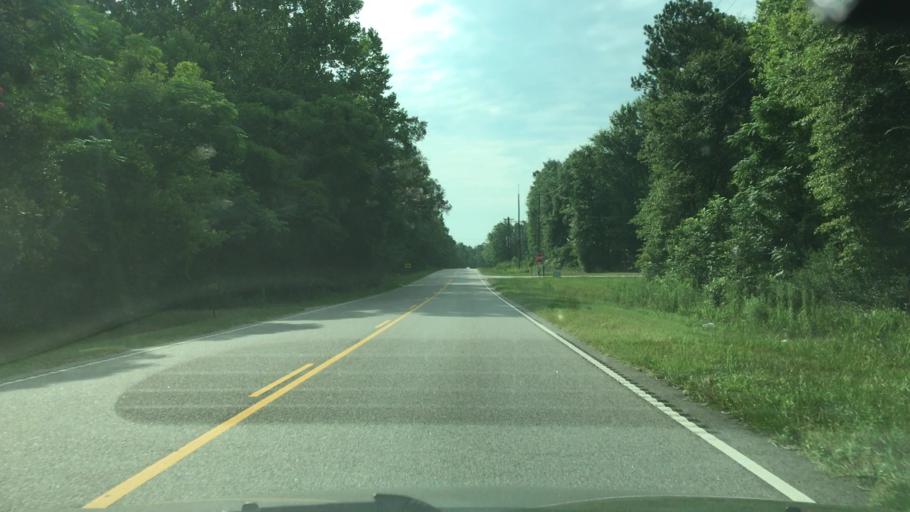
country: US
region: South Carolina
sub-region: Barnwell County
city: Williston
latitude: 33.6591
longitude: -81.3828
